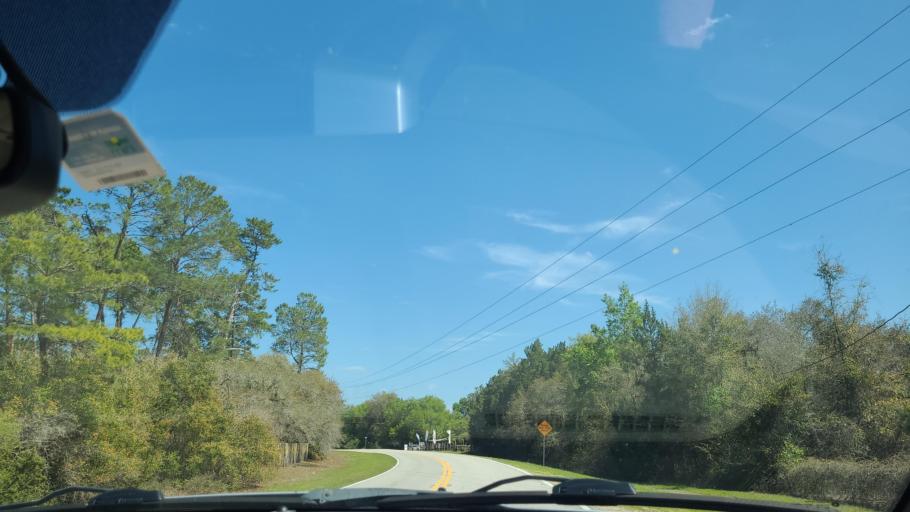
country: US
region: Florida
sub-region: Putnam County
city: Crescent City
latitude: 29.3785
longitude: -81.7668
